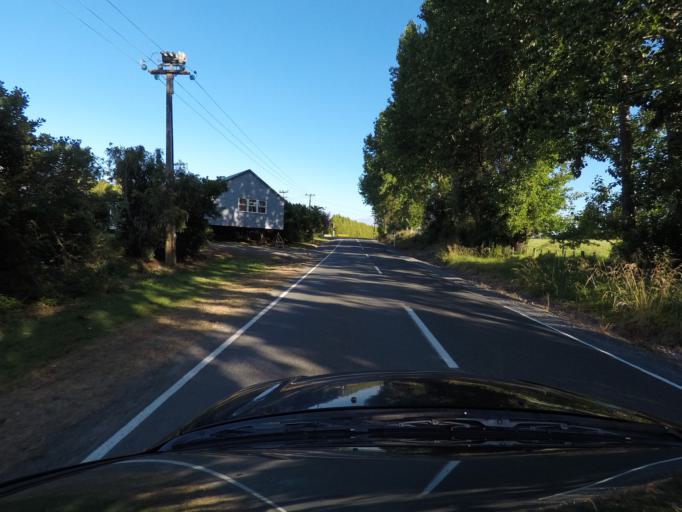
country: NZ
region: Northland
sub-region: Whangarei
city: Whangarei
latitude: -35.6405
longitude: 174.2974
